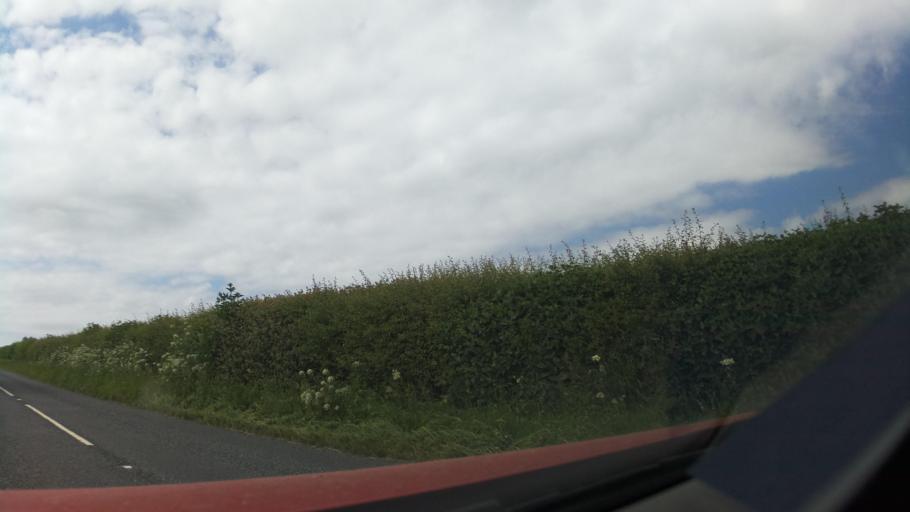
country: GB
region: England
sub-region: Somerset
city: Milborne Port
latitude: 51.0201
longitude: -2.4683
